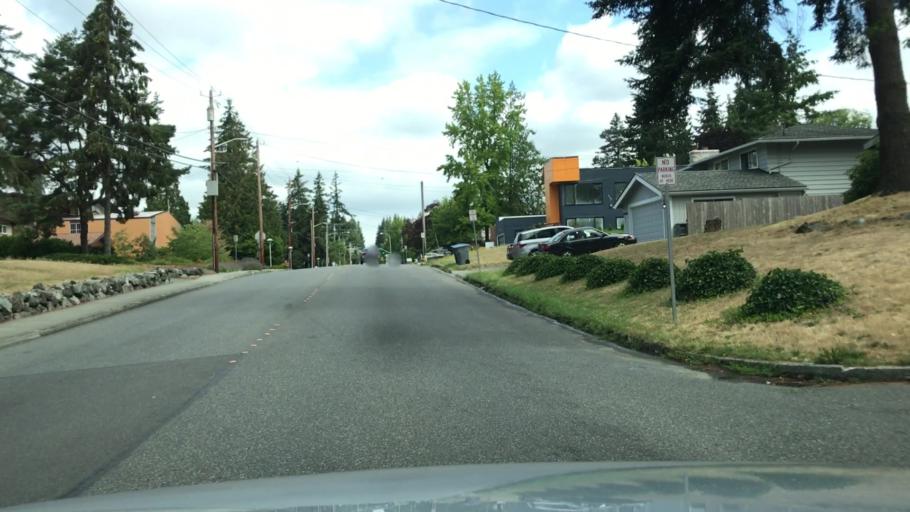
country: US
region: Washington
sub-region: King County
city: Eastgate
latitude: 47.6073
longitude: -122.1322
